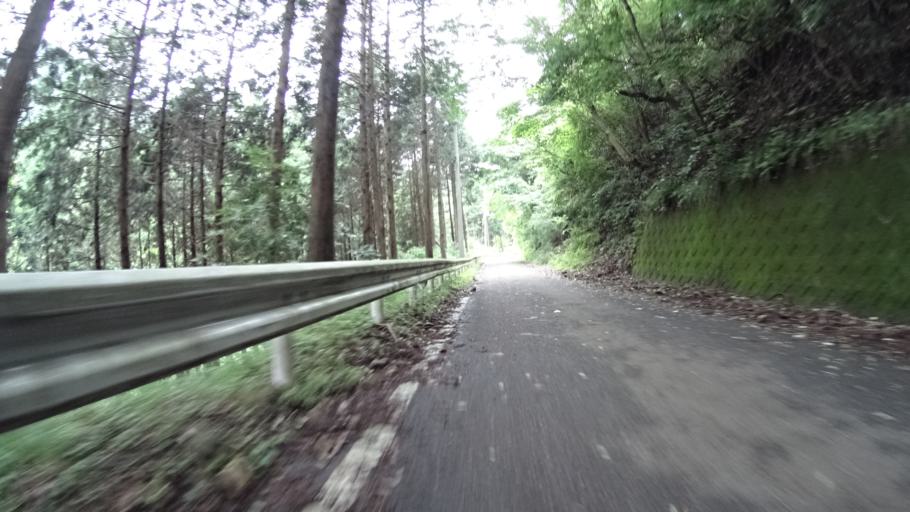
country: JP
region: Kanagawa
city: Atsugi
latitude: 35.5028
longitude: 139.2721
